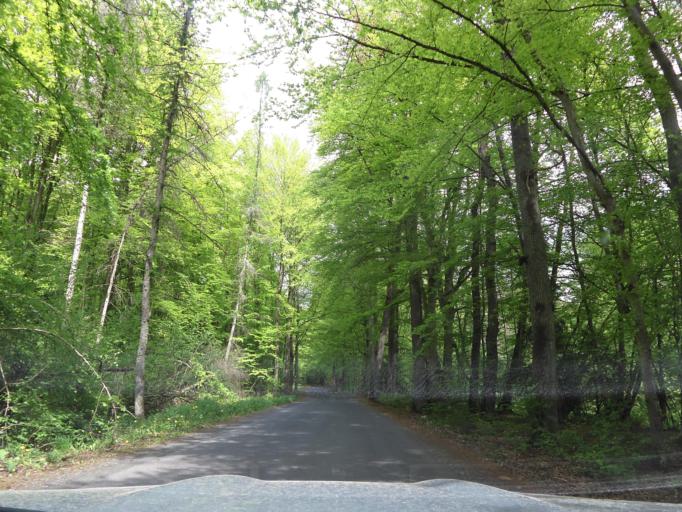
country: DE
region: Hesse
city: Oberbiel
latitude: 50.5712
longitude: 8.4226
